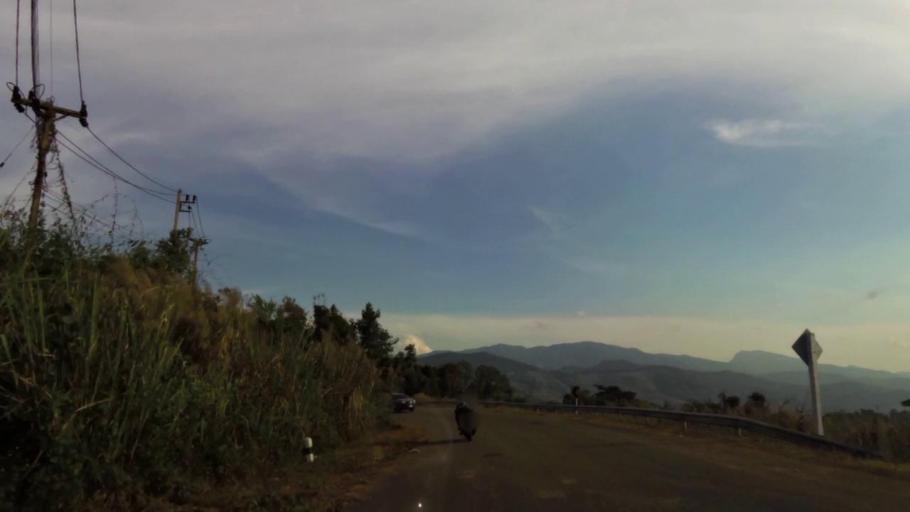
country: TH
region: Chiang Rai
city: Khun Tan
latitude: 19.8531
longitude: 100.3763
